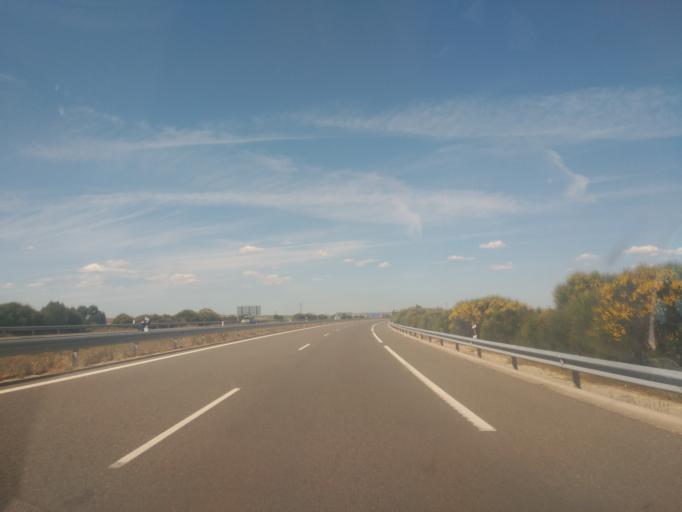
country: ES
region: Castille and Leon
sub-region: Provincia de Salamanca
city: Arapiles
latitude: 40.9042
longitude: -5.6623
